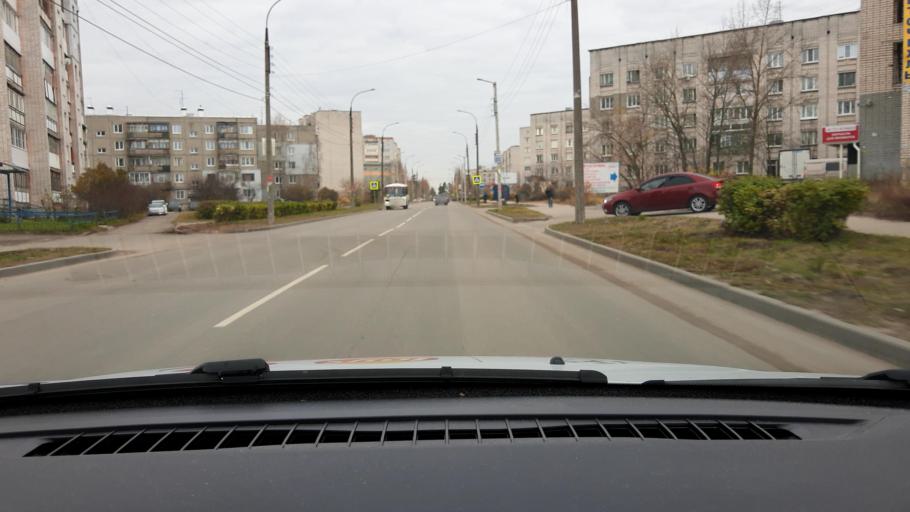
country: RU
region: Nizjnij Novgorod
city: Dzerzhinsk
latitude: 56.2561
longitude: 43.4534
